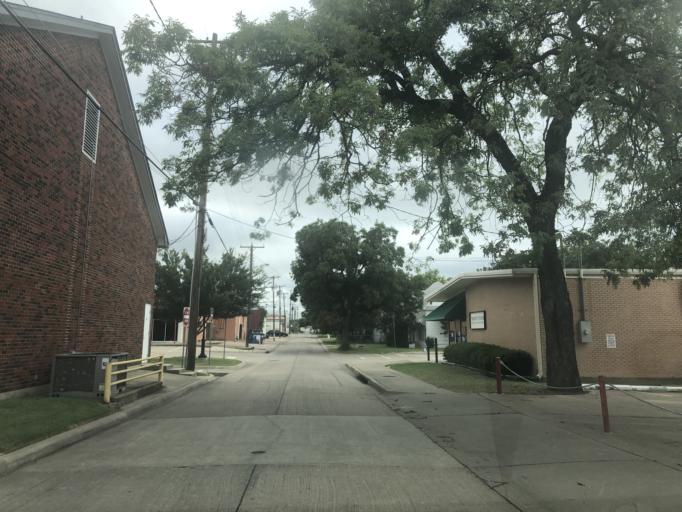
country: US
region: Texas
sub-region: Dallas County
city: Duncanville
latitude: 32.6521
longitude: -96.9079
